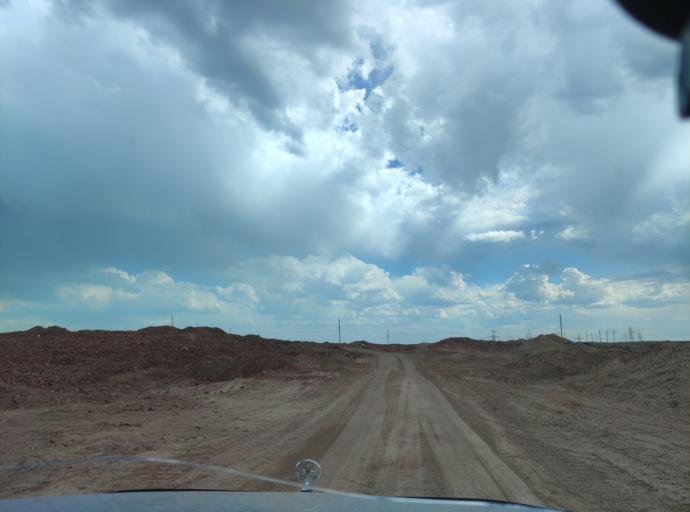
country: KZ
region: Qaraghandy
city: Saryshaghan
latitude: 46.1264
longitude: 73.5966
